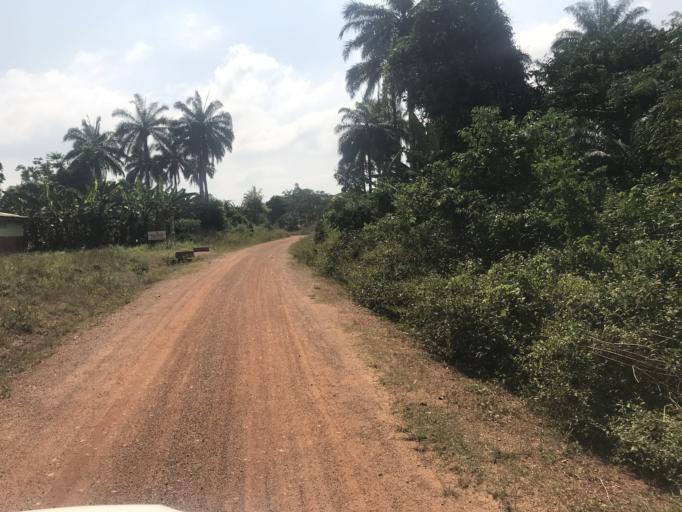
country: NG
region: Osun
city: Iragbiji
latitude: 7.8250
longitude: 4.6407
